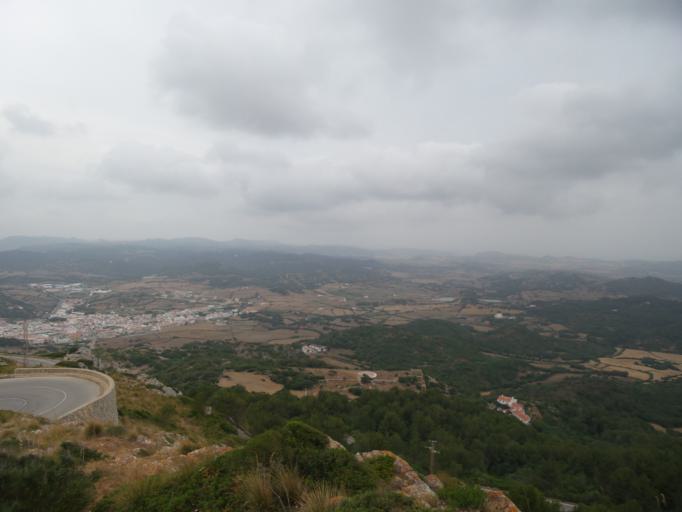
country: ES
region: Balearic Islands
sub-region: Illes Balears
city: Mercadal
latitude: 39.9850
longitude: 4.1124
